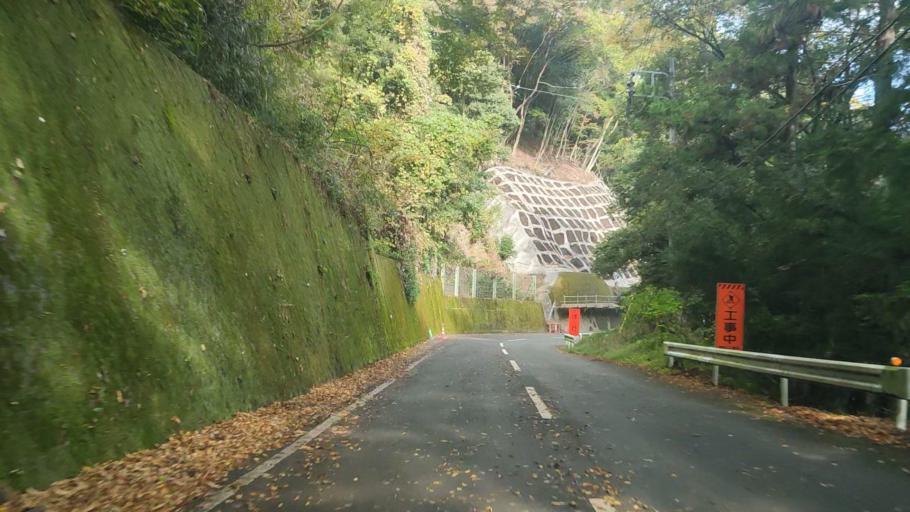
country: JP
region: Shizuoka
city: Fujinomiya
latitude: 35.3468
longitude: 138.4380
